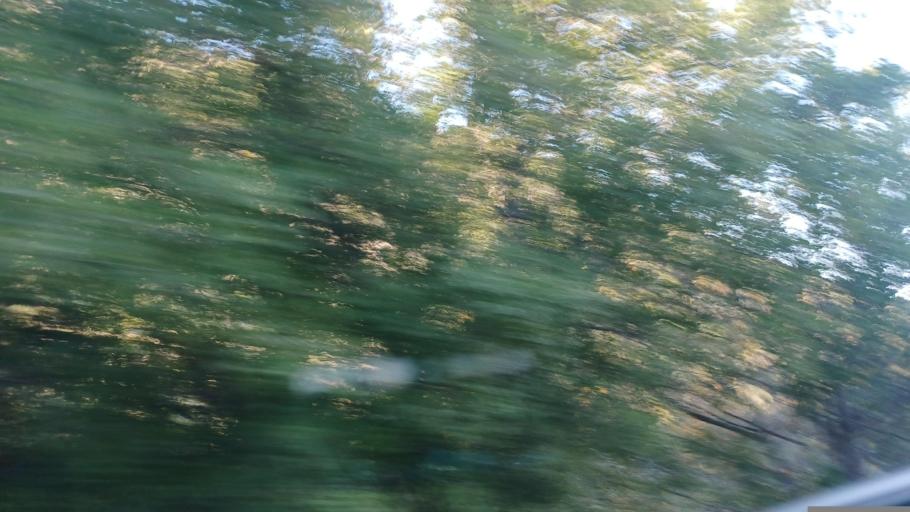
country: CY
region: Pafos
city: Mesogi
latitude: 34.8685
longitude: 32.5763
